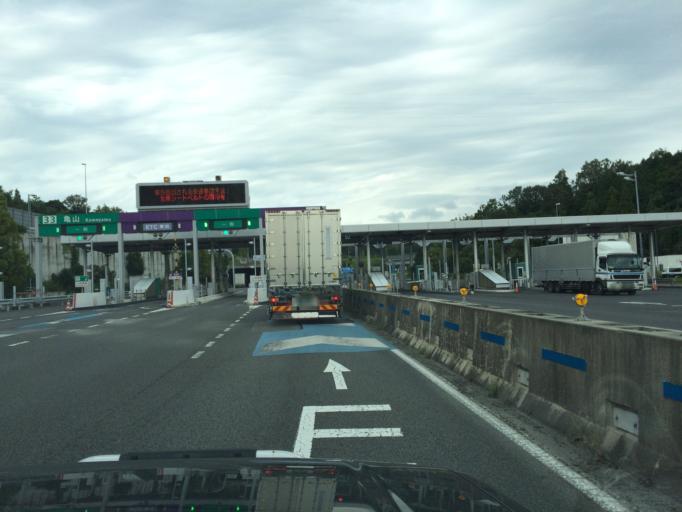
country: JP
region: Mie
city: Kameyama
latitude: 34.8606
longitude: 136.4132
